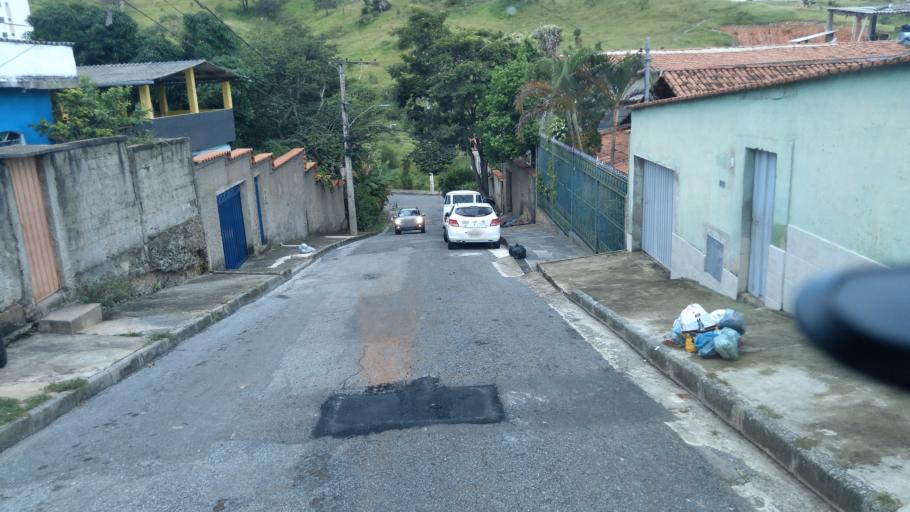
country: BR
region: Minas Gerais
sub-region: Belo Horizonte
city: Belo Horizonte
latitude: -19.8966
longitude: -43.8863
